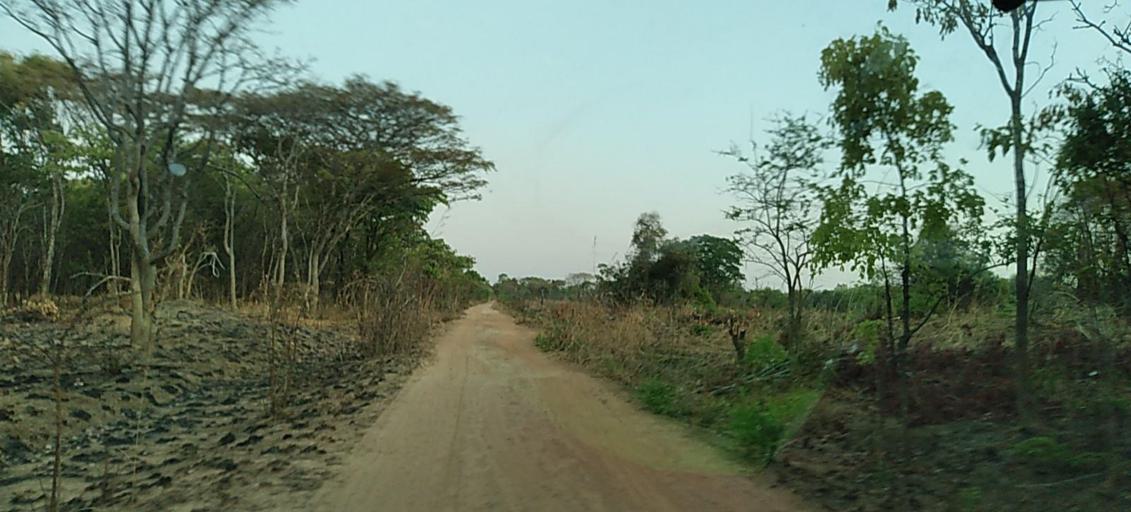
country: ZM
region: North-Western
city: Kalengwa
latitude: -13.1104
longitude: 25.1656
